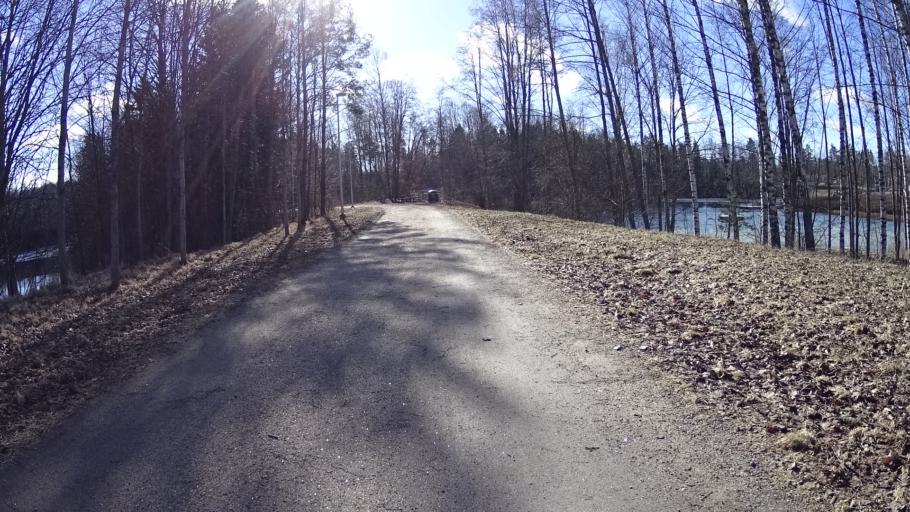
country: FI
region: Uusimaa
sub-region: Helsinki
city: Teekkarikylae
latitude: 60.2717
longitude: 24.8803
